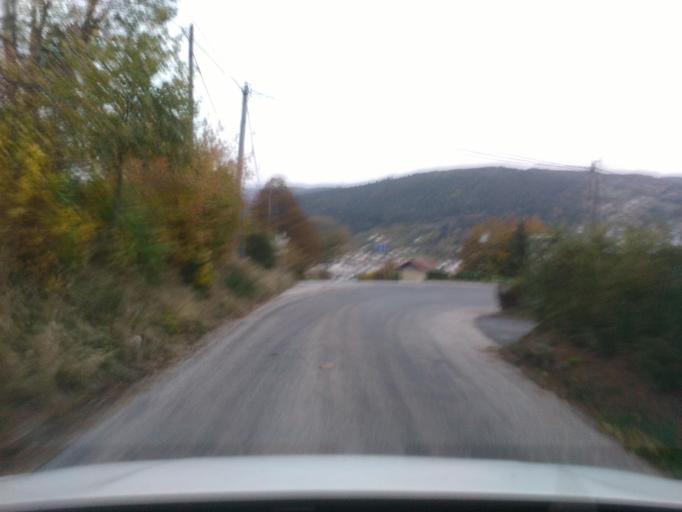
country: FR
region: Lorraine
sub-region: Departement des Vosges
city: Gerardmer
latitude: 48.0804
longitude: 6.8674
